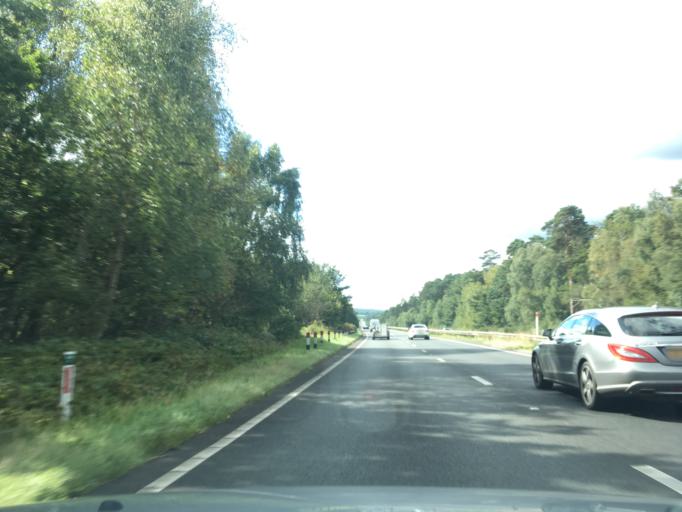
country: GB
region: England
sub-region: Surrey
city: Milford
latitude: 51.1622
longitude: -0.6699
